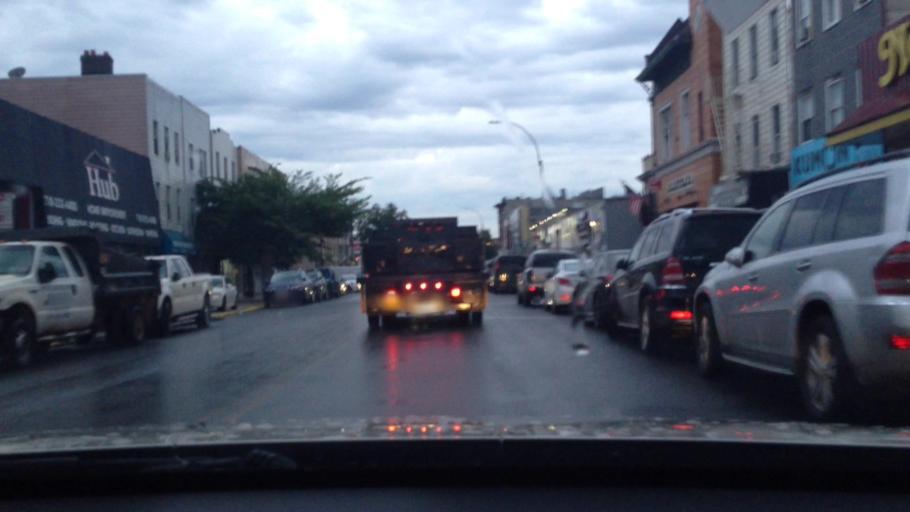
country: US
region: New York
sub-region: Kings County
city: Bensonhurst
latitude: 40.6059
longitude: -74.0040
